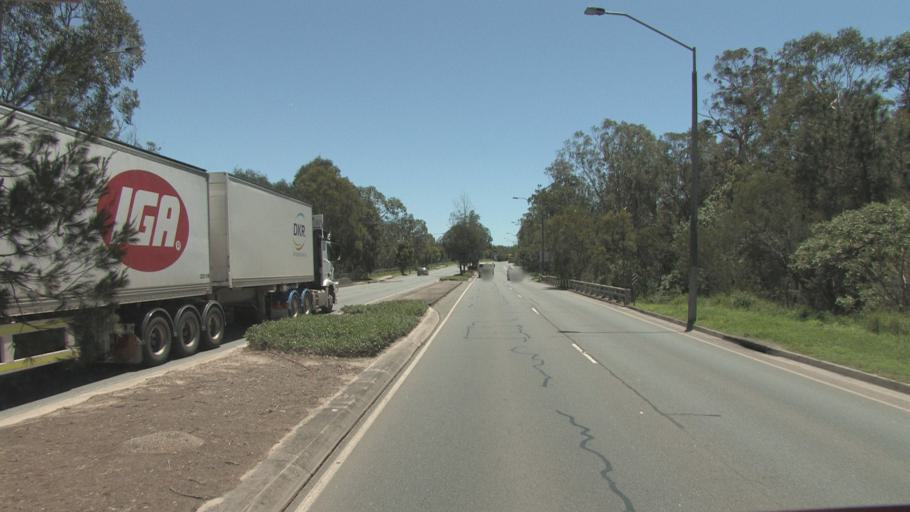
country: AU
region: Queensland
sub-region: Logan
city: Woodridge
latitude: -27.6679
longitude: 153.0682
